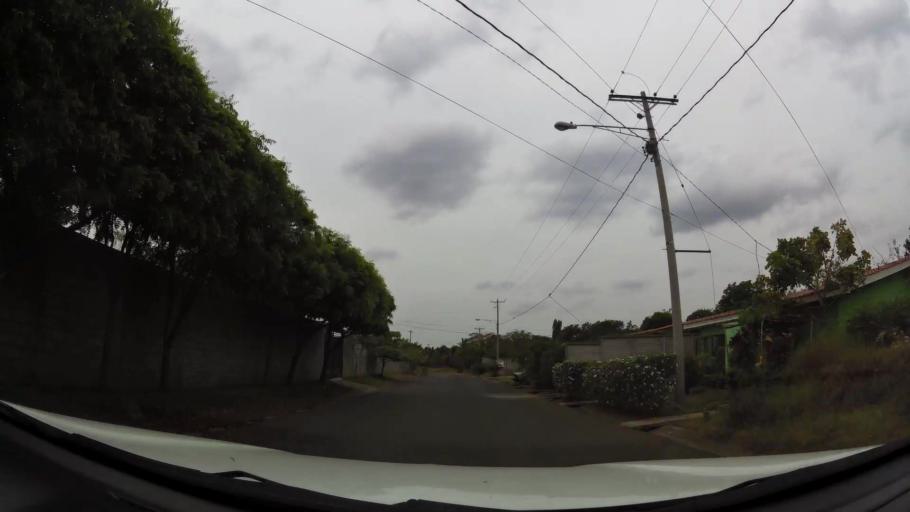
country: NI
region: Masaya
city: Ticuantepe
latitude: 12.0739
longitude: -86.1745
